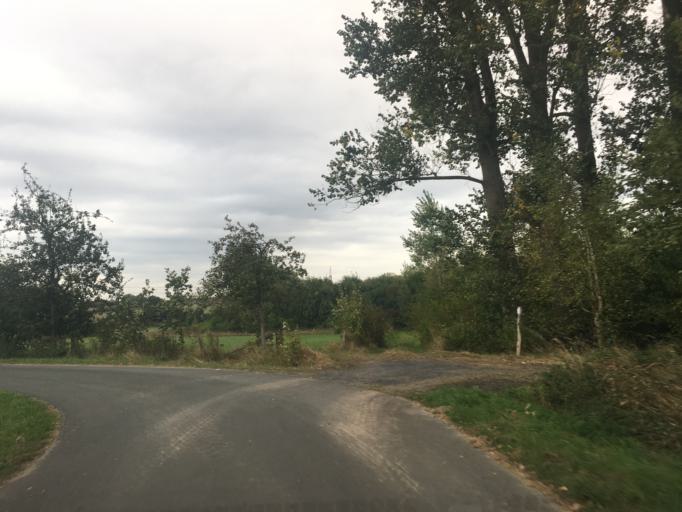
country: DE
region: North Rhine-Westphalia
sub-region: Regierungsbezirk Munster
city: Muenster
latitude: 51.9564
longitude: 7.5527
